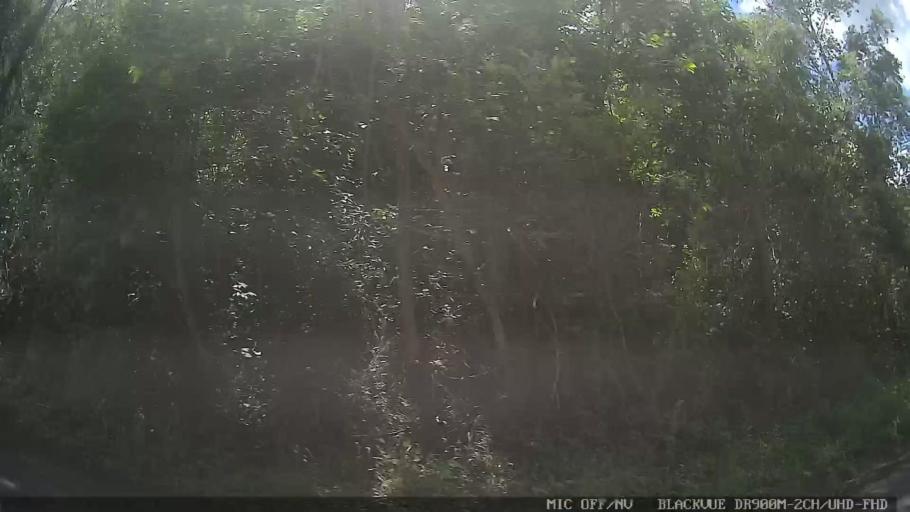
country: BR
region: Sao Paulo
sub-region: Amparo
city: Amparo
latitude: -22.7611
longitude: -46.7512
